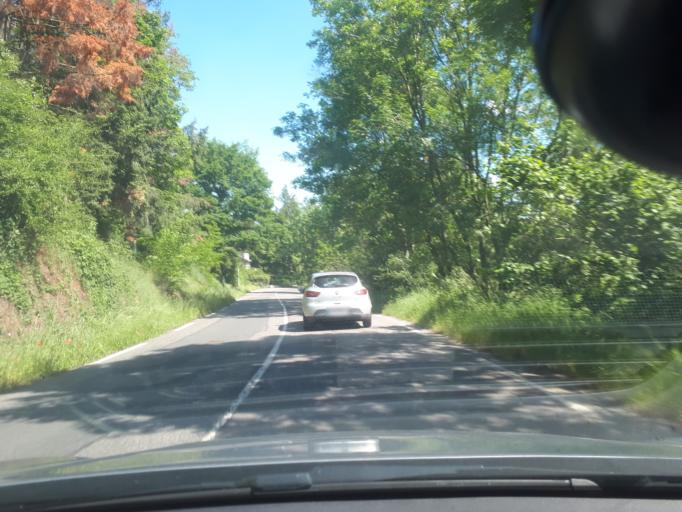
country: FR
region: Rhone-Alpes
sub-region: Departement du Rhone
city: Mornant
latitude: 45.6123
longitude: 4.6748
